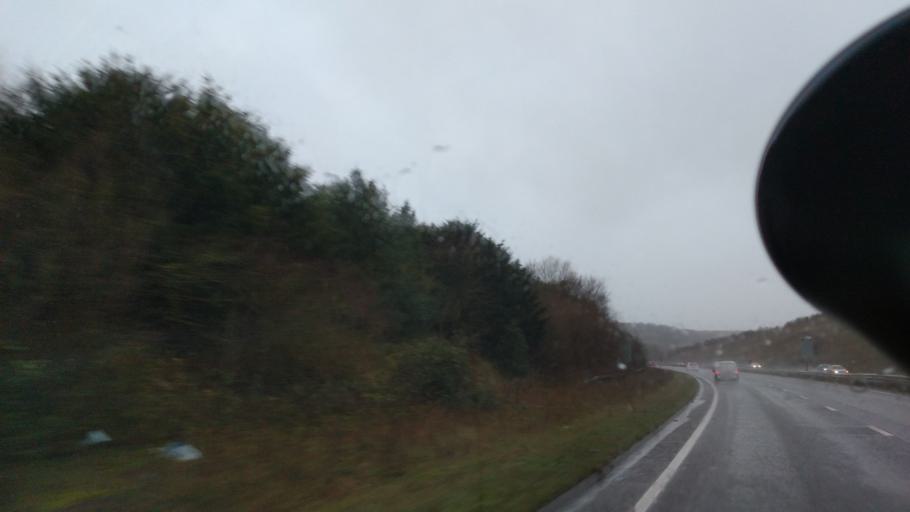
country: GB
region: England
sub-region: East Sussex
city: Portslade
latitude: 50.8580
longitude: -0.2281
